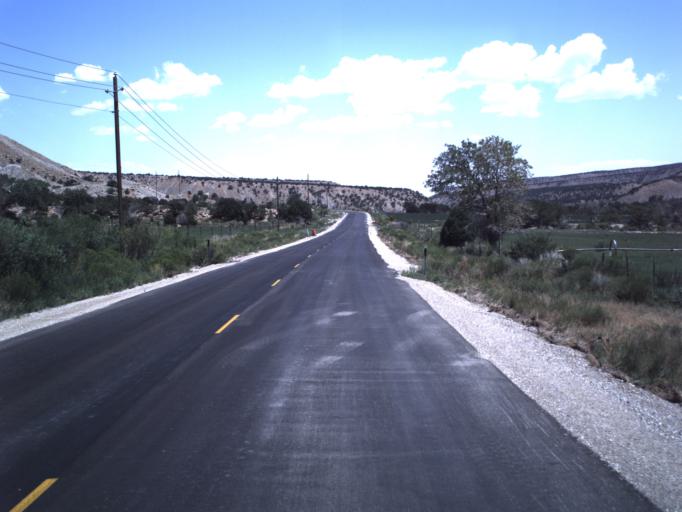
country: US
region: Utah
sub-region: Emery County
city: Orangeville
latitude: 39.2759
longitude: -111.1718
